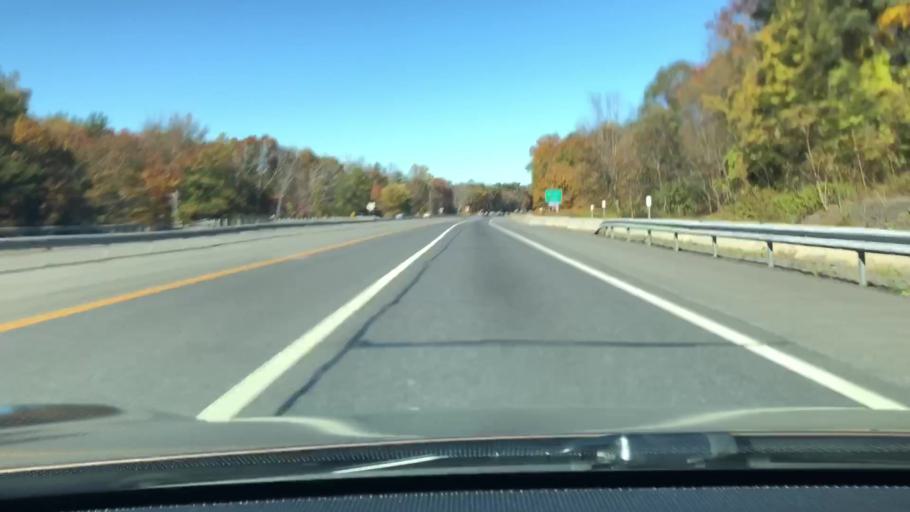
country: US
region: New York
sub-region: Ulster County
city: Tillson
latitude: 41.8162
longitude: -74.0557
